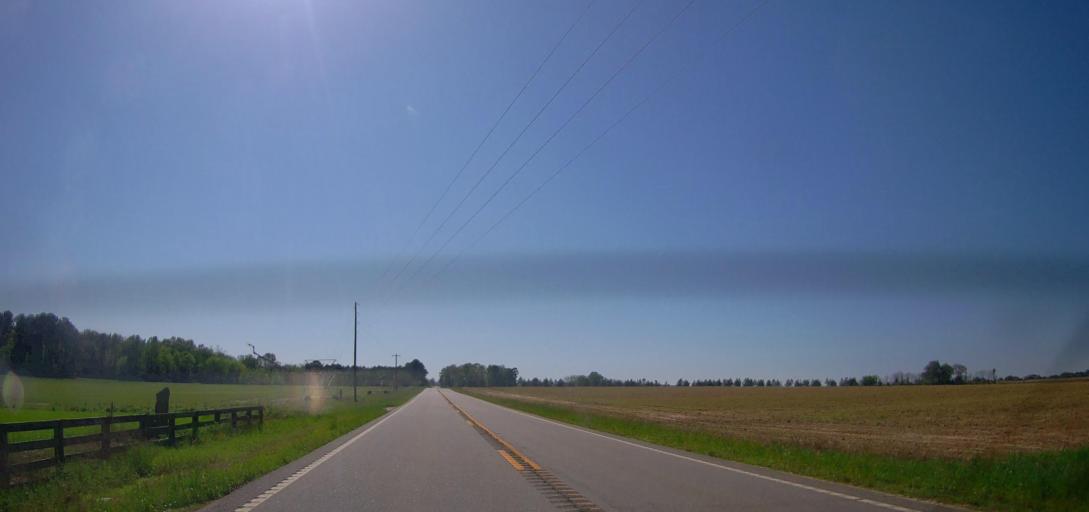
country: US
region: Georgia
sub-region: Dooly County
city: Unadilla
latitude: 32.2602
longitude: -83.7062
